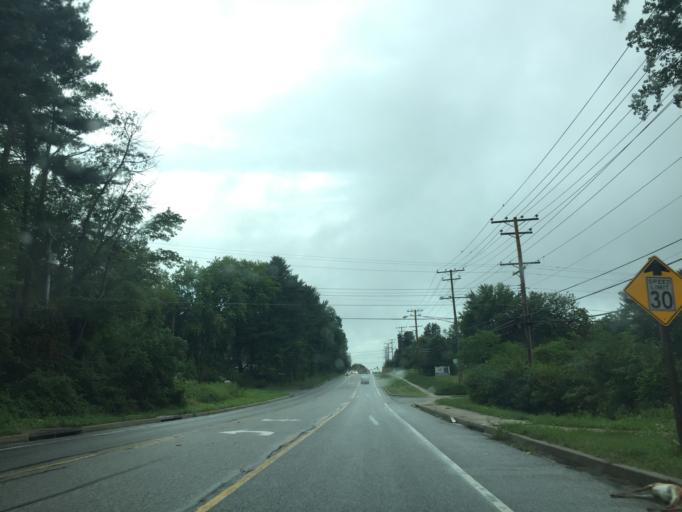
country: US
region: Maryland
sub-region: Harford County
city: South Bel Air
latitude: 39.5232
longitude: -76.3373
